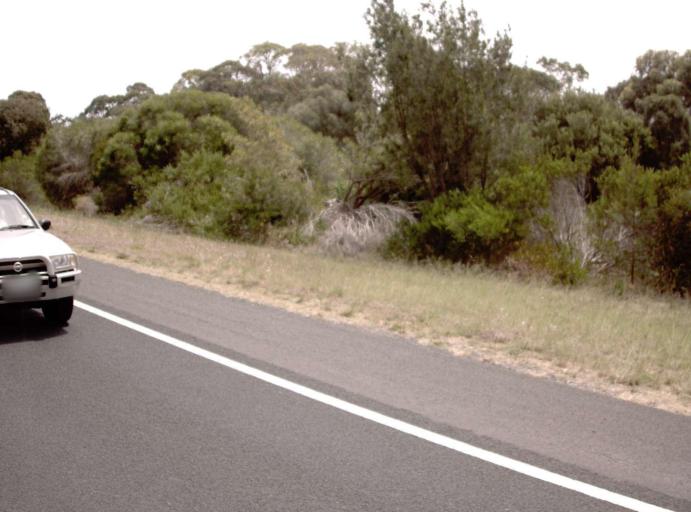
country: AU
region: Victoria
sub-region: Mornington Peninsula
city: Rosebud West
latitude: -38.3747
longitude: 144.8945
